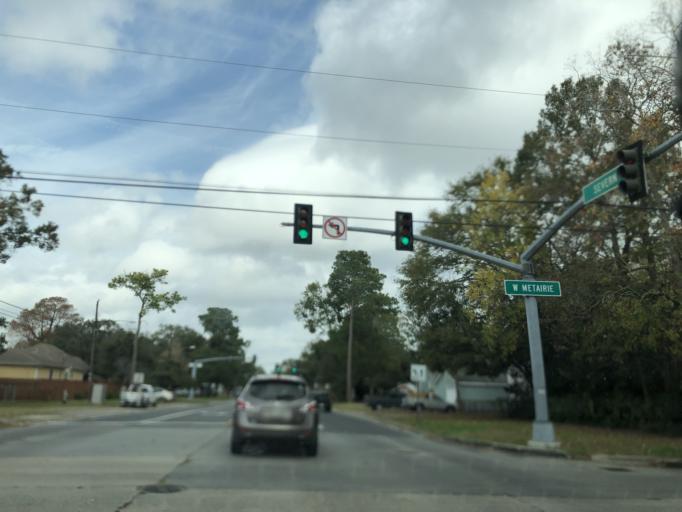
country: US
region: Louisiana
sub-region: Jefferson Parish
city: Metairie Terrace
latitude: 29.9813
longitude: -90.1603
